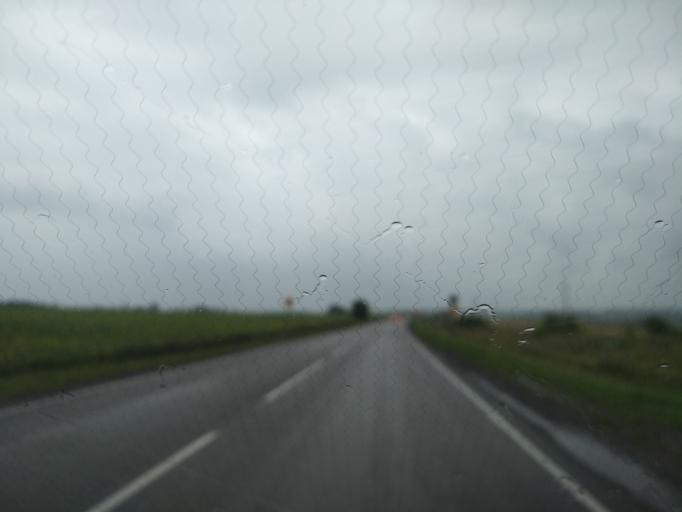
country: RU
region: Voronezj
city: Orlovo
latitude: 51.6785
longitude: 39.7929
